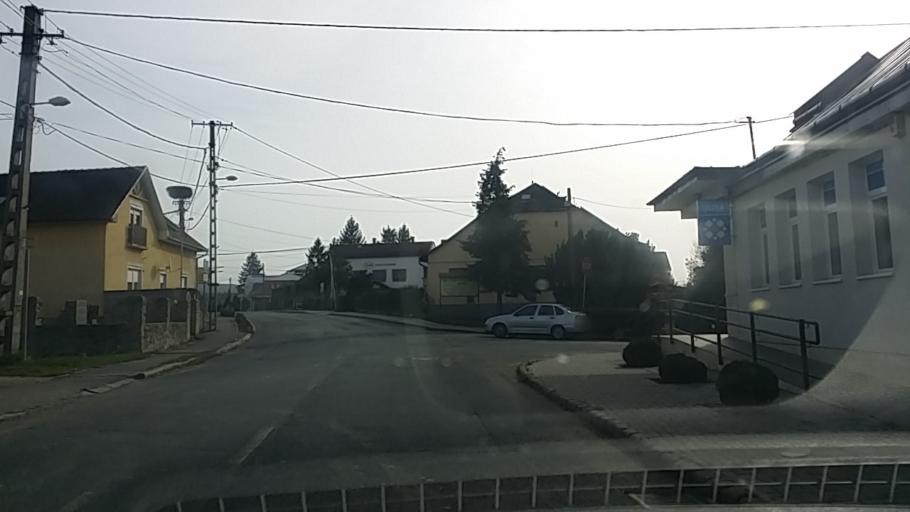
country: HU
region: Borsod-Abauj-Zemplen
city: Sarospatak
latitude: 48.4723
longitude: 21.5095
